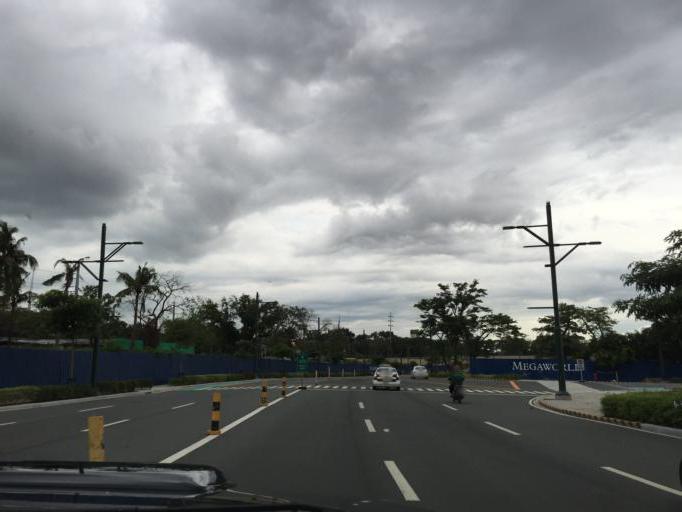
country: PH
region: Metro Manila
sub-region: Makati City
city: Makati City
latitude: 14.5383
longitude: 121.0461
